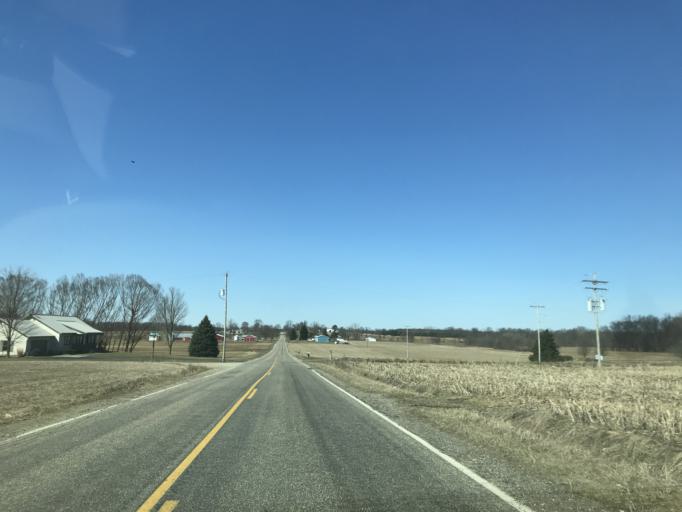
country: US
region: Michigan
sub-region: Hillsdale County
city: Jonesville
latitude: 41.9855
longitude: -84.6988
